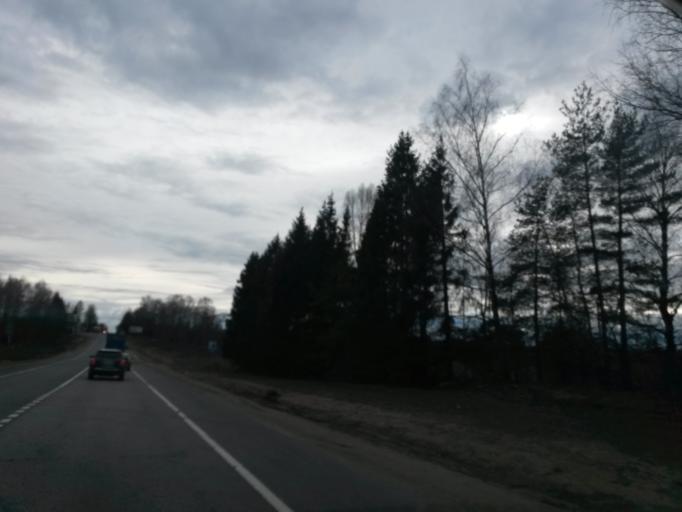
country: RU
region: Jaroslavl
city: Petrovsk
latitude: 56.9020
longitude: 39.1131
